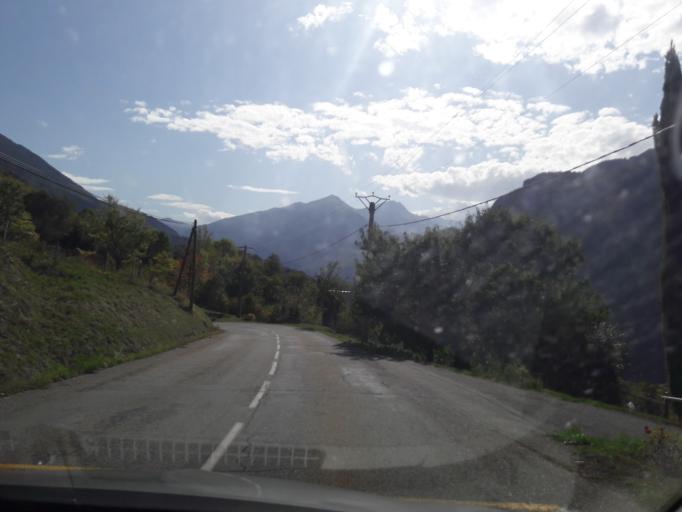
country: FR
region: Rhone-Alpes
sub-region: Departement de la Savoie
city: Saint-Jean-de-Maurienne
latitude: 45.3174
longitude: 6.3488
